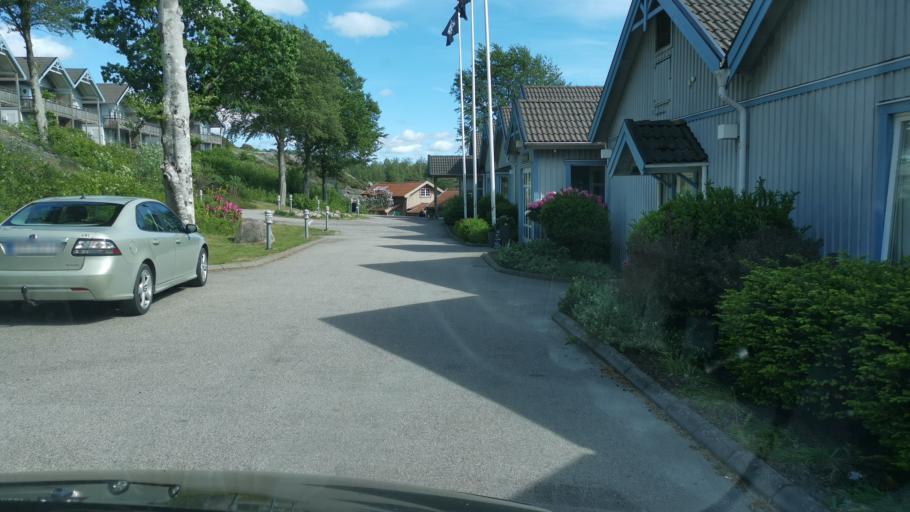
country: SE
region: Vaestra Goetaland
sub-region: Orust
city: Henan
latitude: 58.2611
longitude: 11.5988
